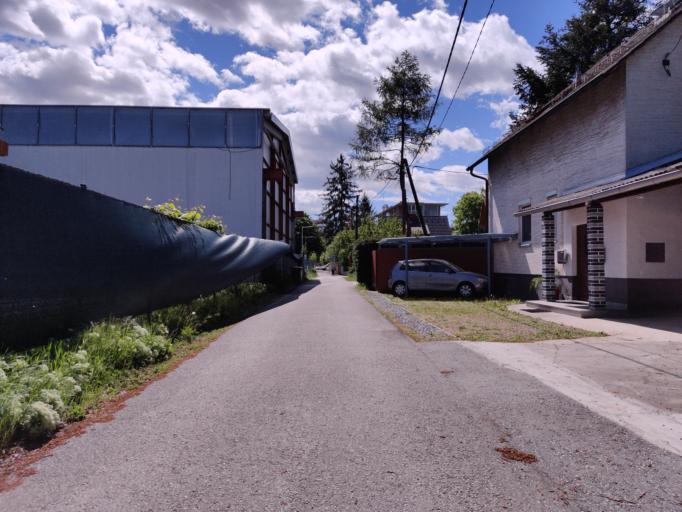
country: AT
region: Styria
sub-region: Graz Stadt
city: Goesting
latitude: 47.0809
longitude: 15.4083
